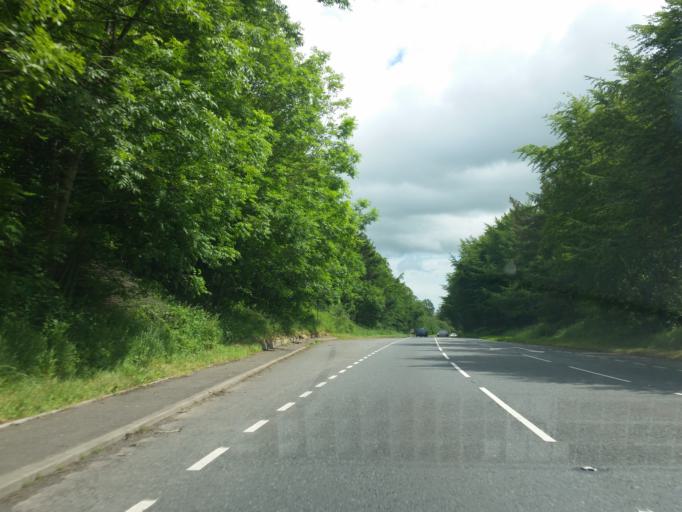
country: IE
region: Ulster
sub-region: County Monaghan
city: Monaghan
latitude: 54.4722
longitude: -7.0529
